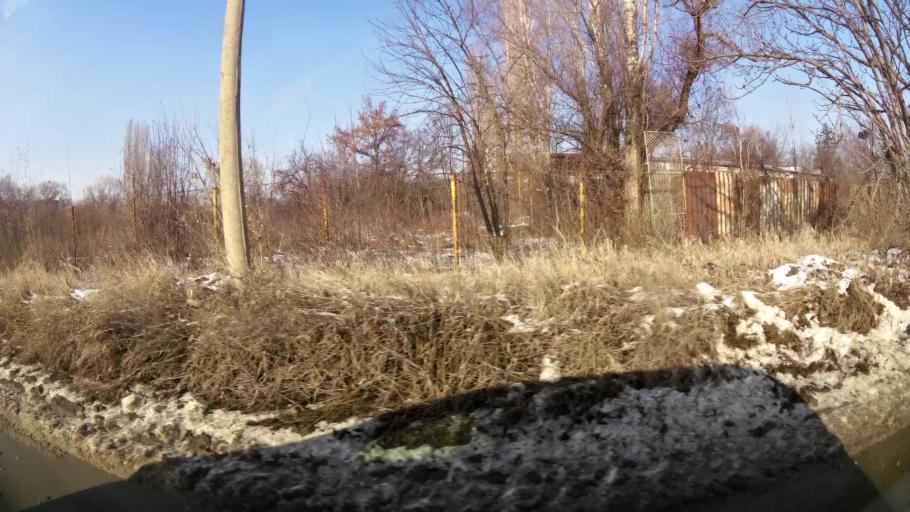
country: BG
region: Sofia-Capital
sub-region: Stolichna Obshtina
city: Sofia
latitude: 42.6568
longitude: 23.3238
